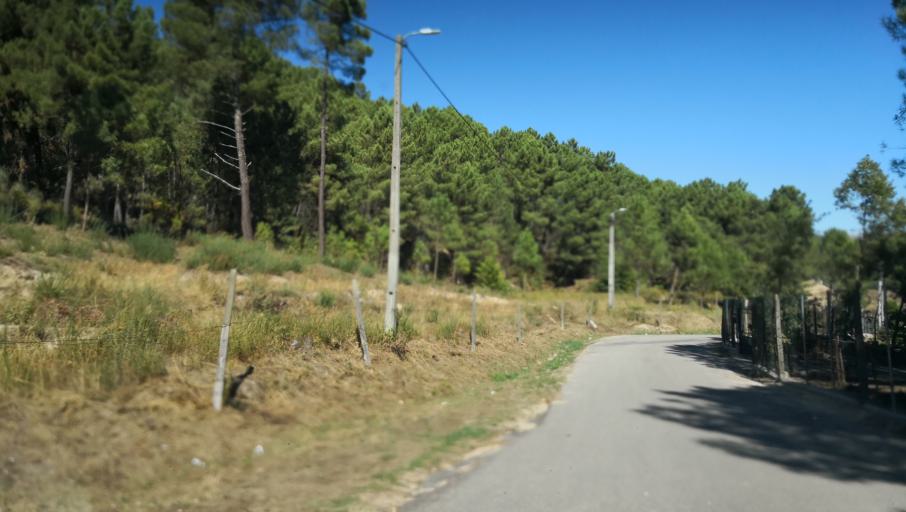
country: PT
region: Vila Real
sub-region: Vila Real
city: Vila Real
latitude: 41.3190
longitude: -7.7256
